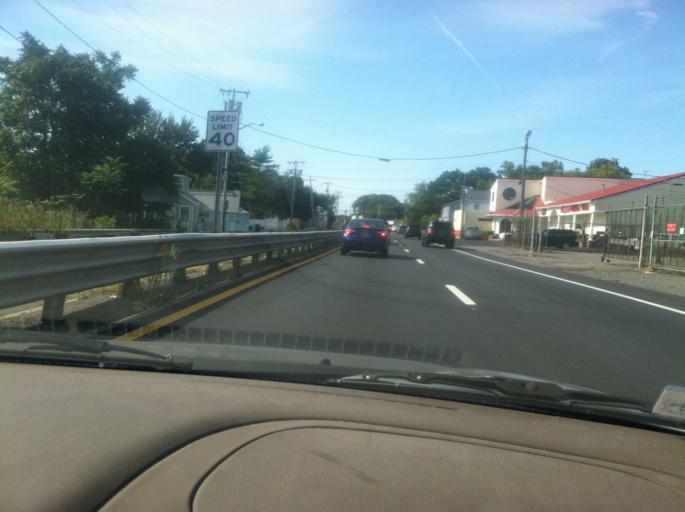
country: US
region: Massachusetts
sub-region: Suffolk County
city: Revere
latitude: 42.4269
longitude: -70.9842
